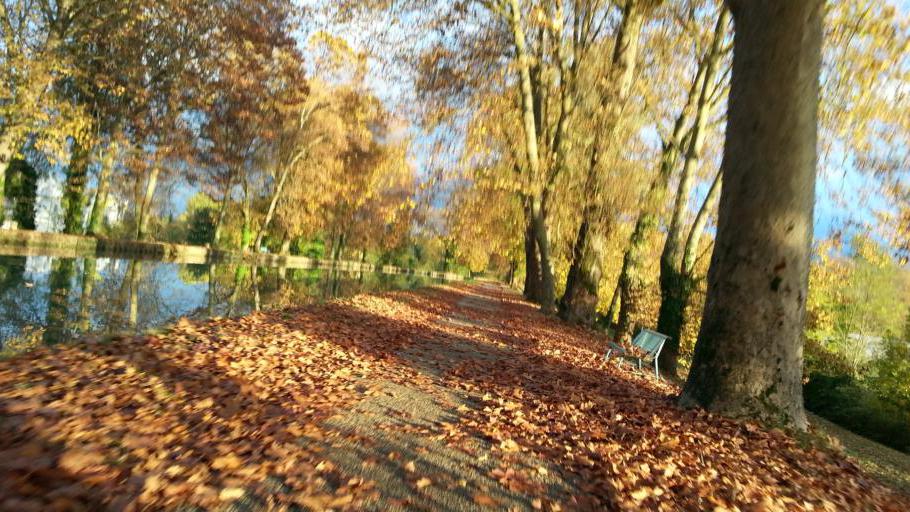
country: FR
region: Midi-Pyrenees
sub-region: Departement du Tarn-et-Garonne
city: Moissac
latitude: 44.0975
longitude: 1.1001
